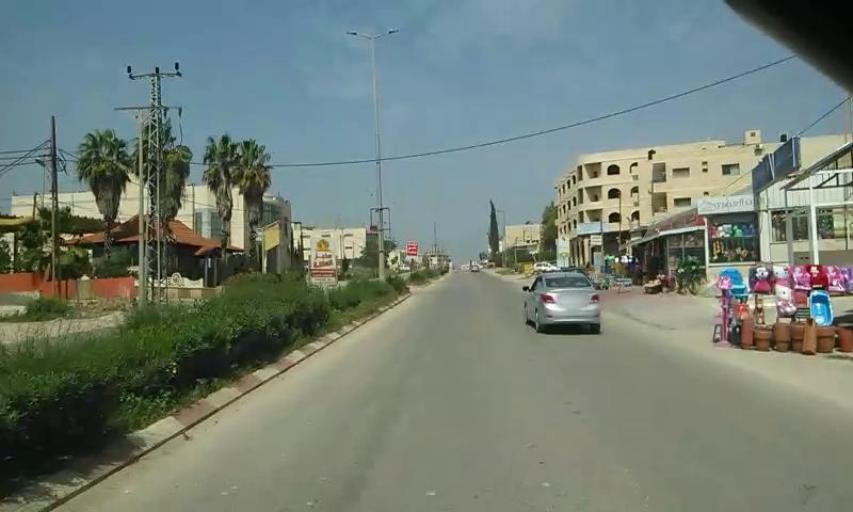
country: PS
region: West Bank
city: Janin
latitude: 32.4822
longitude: 35.2993
